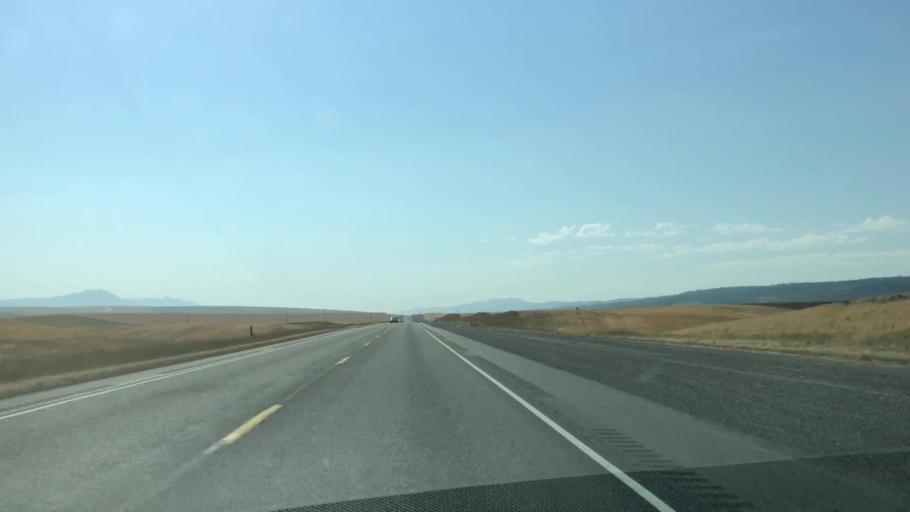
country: US
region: Idaho
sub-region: Madison County
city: Rexburg
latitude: 43.5543
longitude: -111.5356
